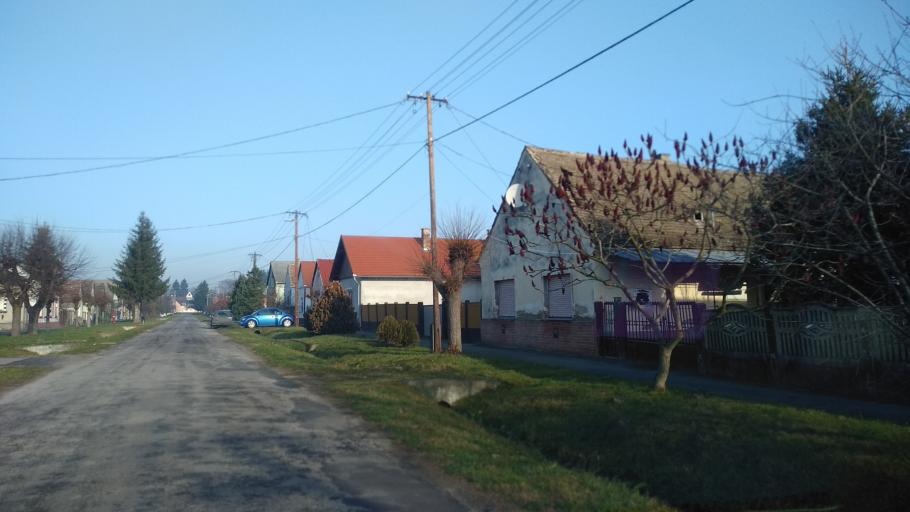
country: HU
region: Somogy
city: Barcs
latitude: 45.9629
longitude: 17.4746
